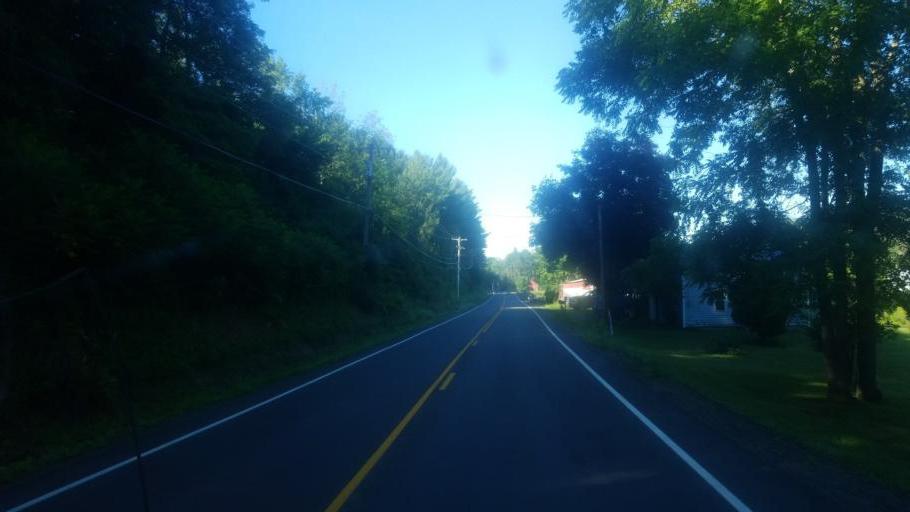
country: US
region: New York
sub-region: Wayne County
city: Newark
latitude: 43.0704
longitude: -77.0793
